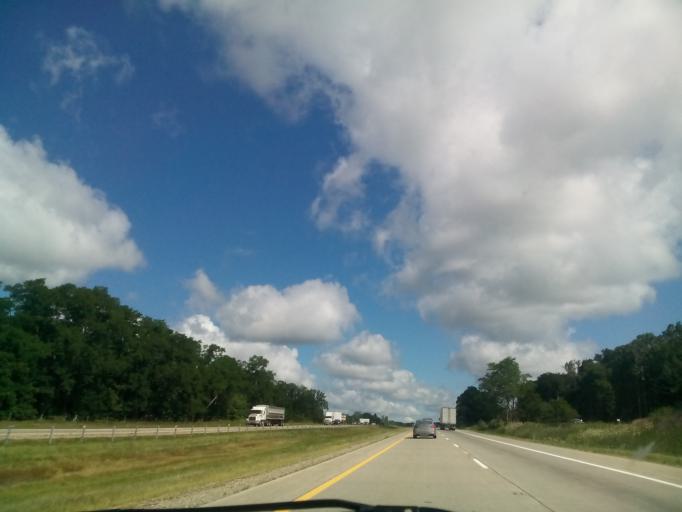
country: US
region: Michigan
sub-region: Genesee County
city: Fenton
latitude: 42.7181
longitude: -83.7626
